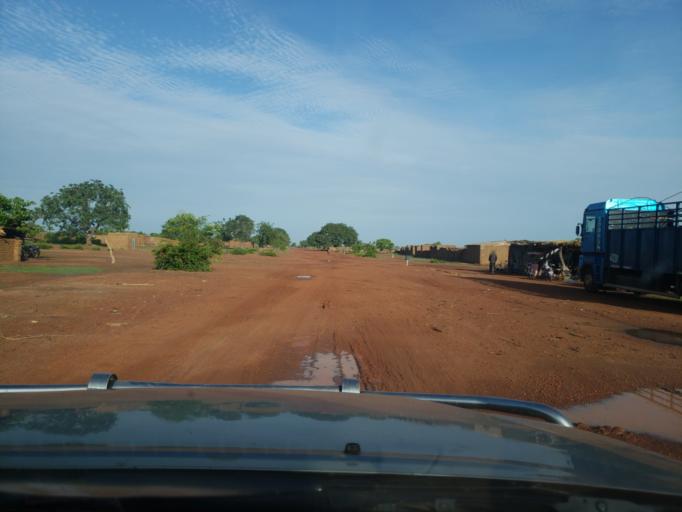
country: ML
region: Sikasso
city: Koutiala
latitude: 12.4295
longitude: -5.6099
